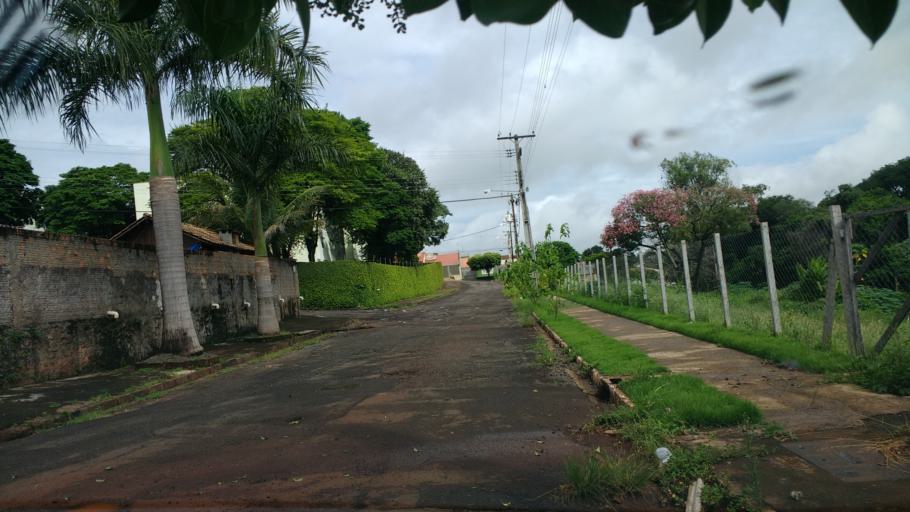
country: BR
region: Parana
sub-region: Londrina
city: Londrina
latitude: -23.3089
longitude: -51.2080
